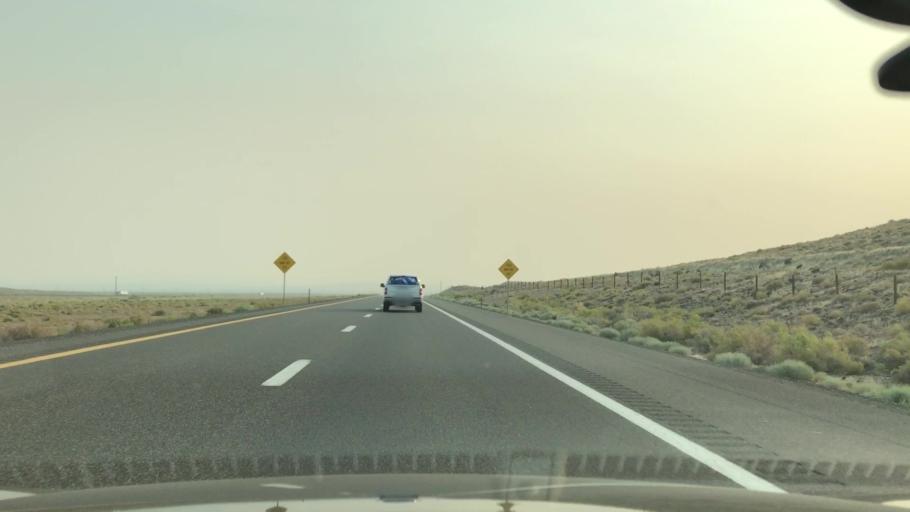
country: US
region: Nevada
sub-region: Lyon County
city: Fernley
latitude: 39.7684
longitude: -119.0367
